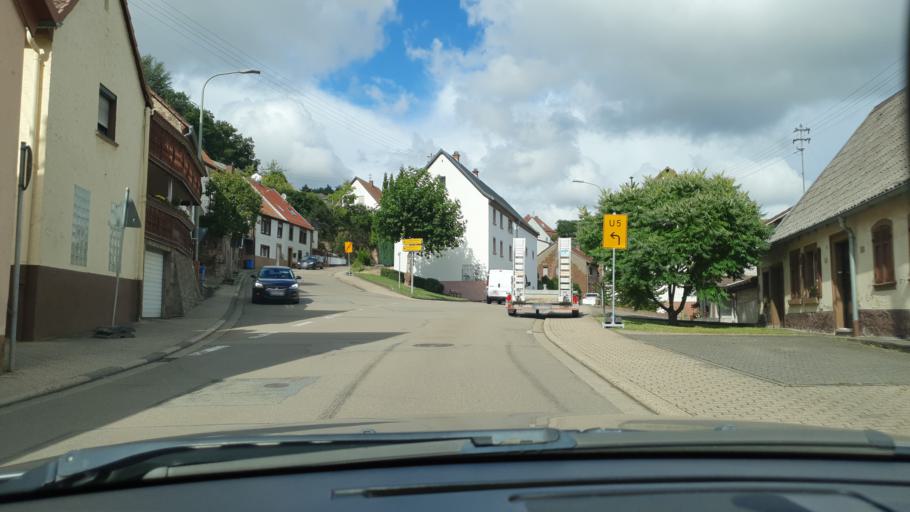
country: DE
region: Rheinland-Pfalz
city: Rieschweiler-Muhlbach
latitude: 49.2483
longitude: 7.5051
